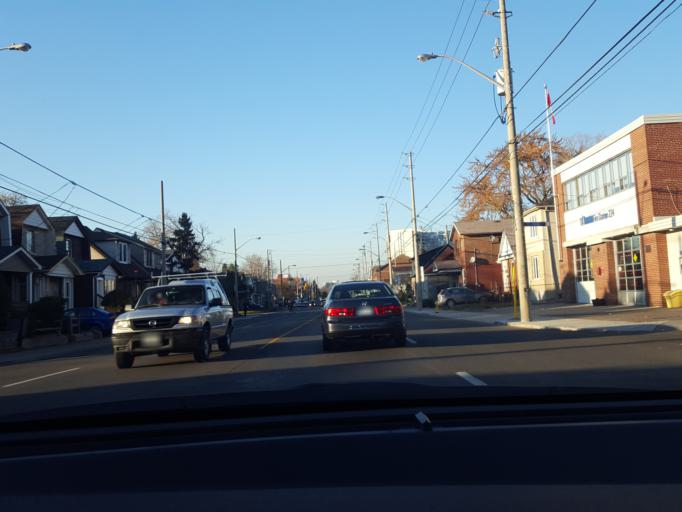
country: CA
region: Ontario
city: Scarborough
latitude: 43.6949
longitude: -79.3167
